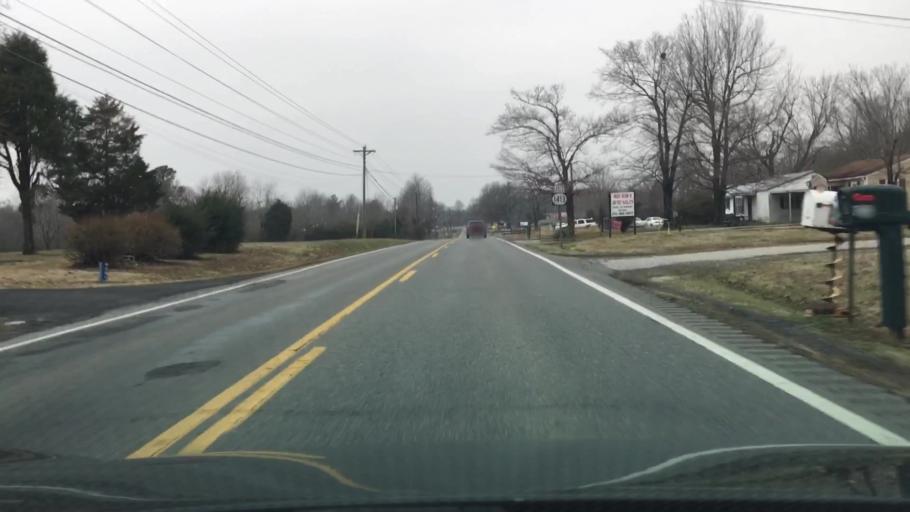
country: US
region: Kentucky
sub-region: Marshall County
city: Calvert City
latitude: 36.9722
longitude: -88.3946
